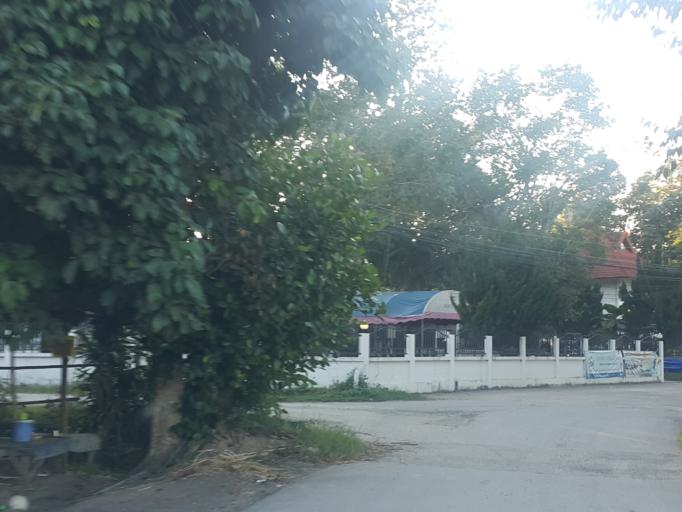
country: TH
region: Chiang Mai
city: San Sai
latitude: 18.8705
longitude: 99.1526
